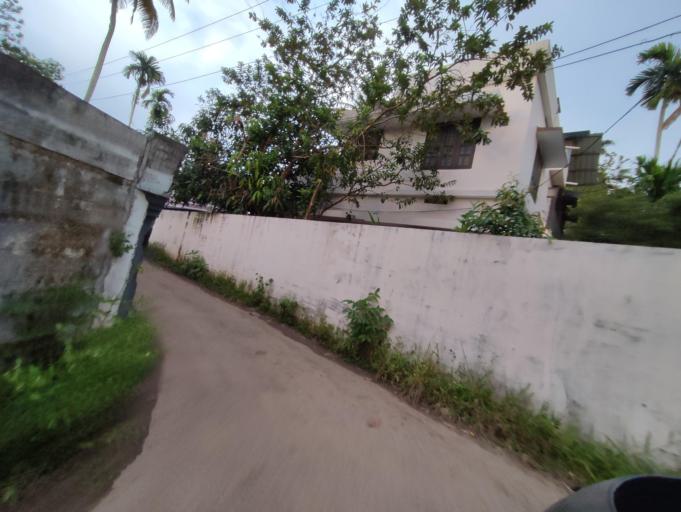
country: IN
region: Kerala
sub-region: Alappuzha
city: Vayalar
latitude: 9.6934
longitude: 76.3362
